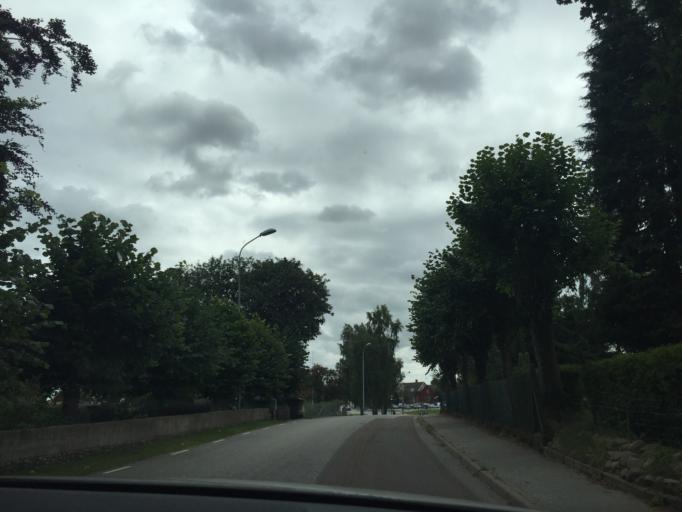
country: SE
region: Skane
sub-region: Sjobo Kommun
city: Blentarp
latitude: 55.5855
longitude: 13.6011
